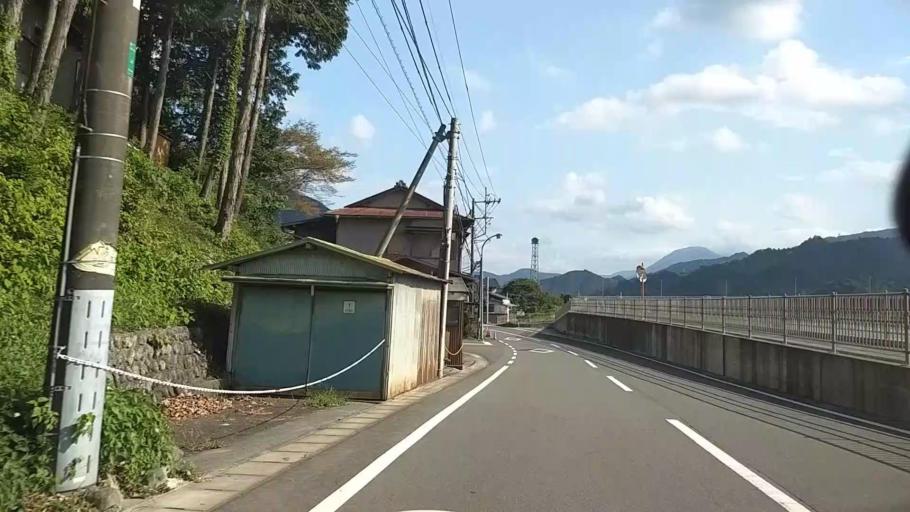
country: JP
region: Shizuoka
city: Fujinomiya
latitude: 35.2858
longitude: 138.4604
